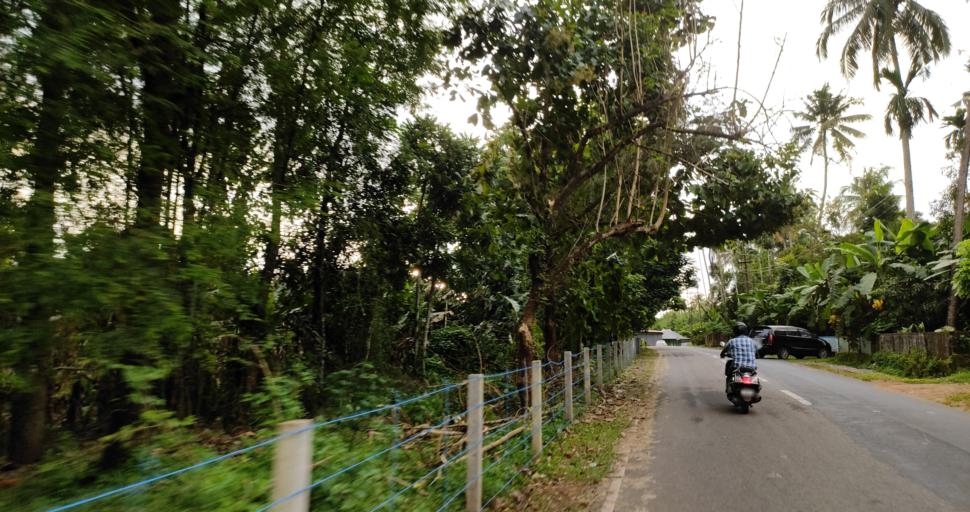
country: IN
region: Kerala
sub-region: Thrissur District
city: Kizhake Chalakudi
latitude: 10.3118
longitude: 76.3900
